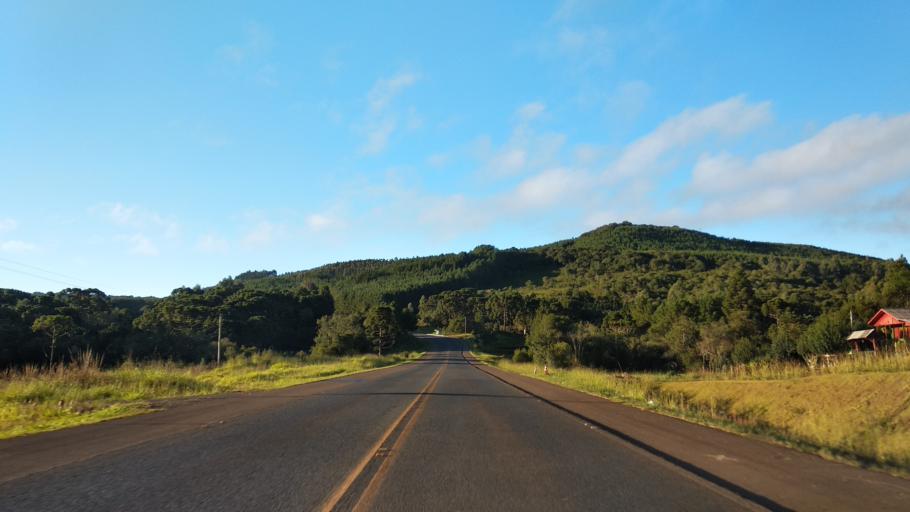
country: BR
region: Santa Catarina
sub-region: Curitibanos
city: Curitibanos
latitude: -27.5987
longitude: -50.7300
